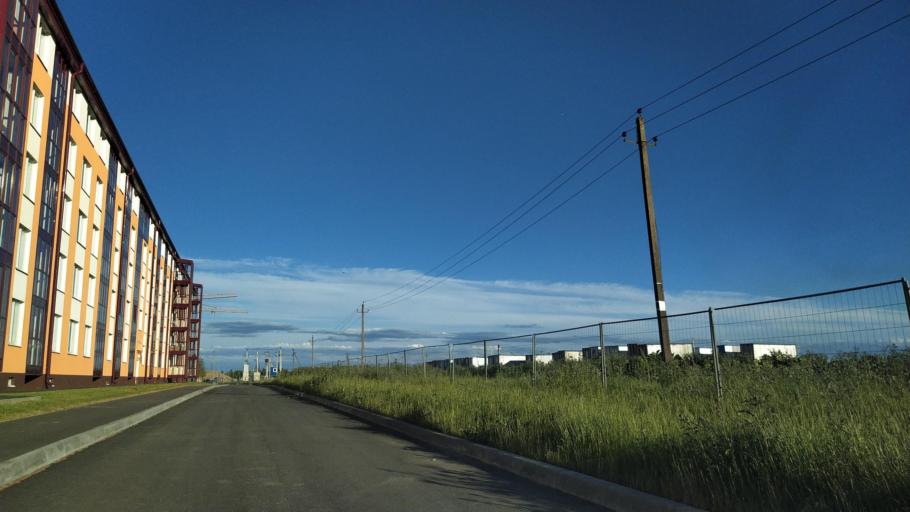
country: RU
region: St.-Petersburg
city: Aleksandrovskaya
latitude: 59.7540
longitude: 30.3581
